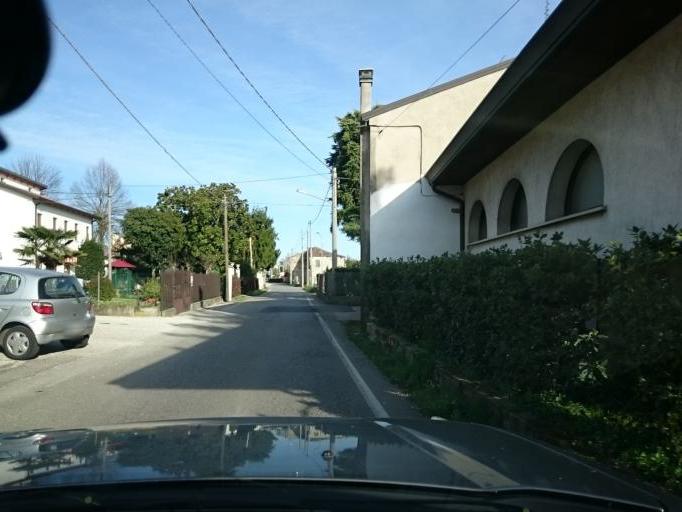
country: IT
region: Veneto
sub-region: Provincia di Padova
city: Mandriola-Sant'Agostino
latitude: 45.3667
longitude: 11.8679
